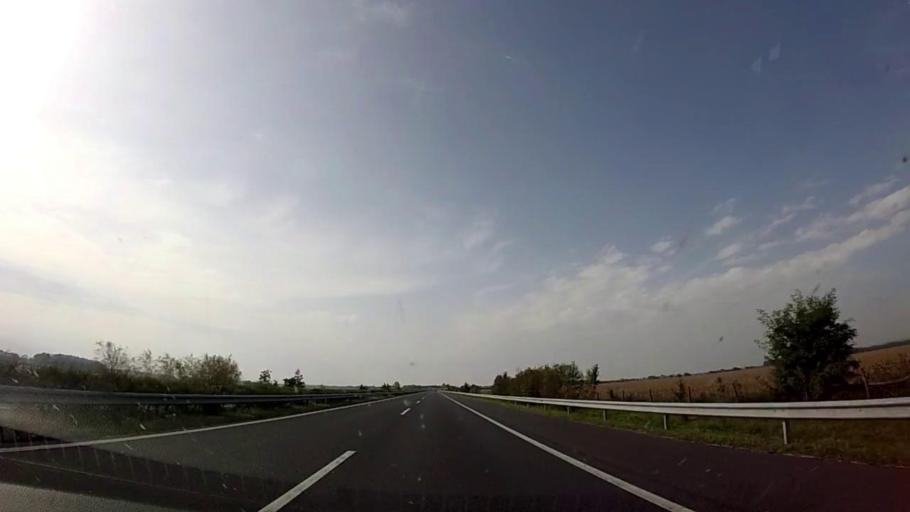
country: HU
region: Zala
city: Becsehely
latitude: 46.4260
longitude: 16.7805
